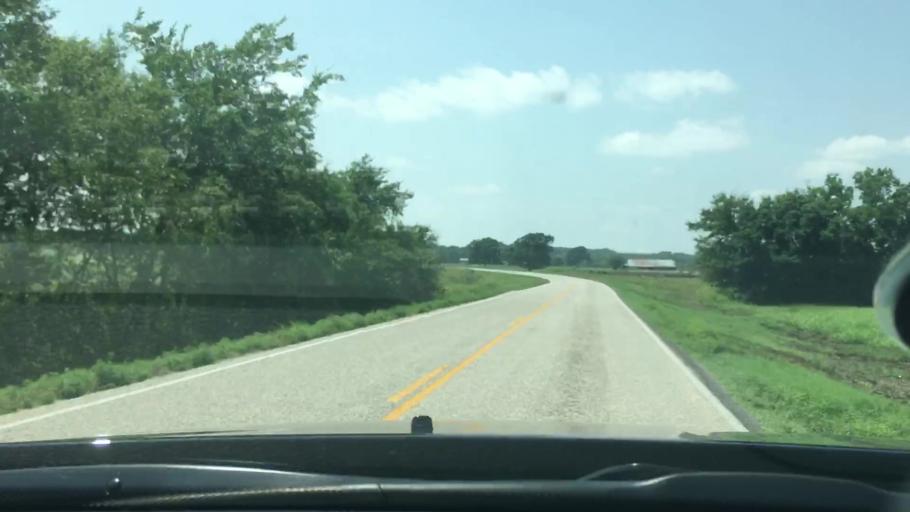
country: US
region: Oklahoma
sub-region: Johnston County
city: Tishomingo
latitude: 34.3762
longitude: -96.4886
